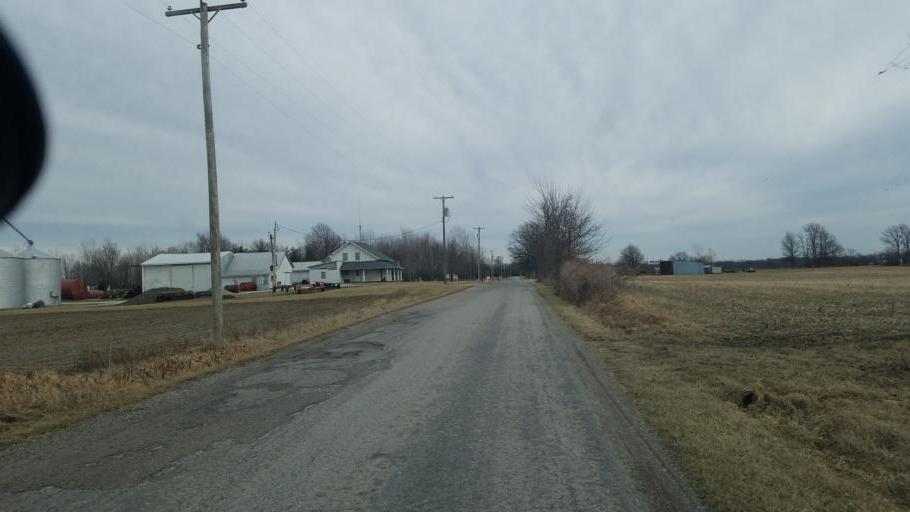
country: US
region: Ohio
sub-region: Delaware County
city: Ashley
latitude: 40.4546
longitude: -82.9800
